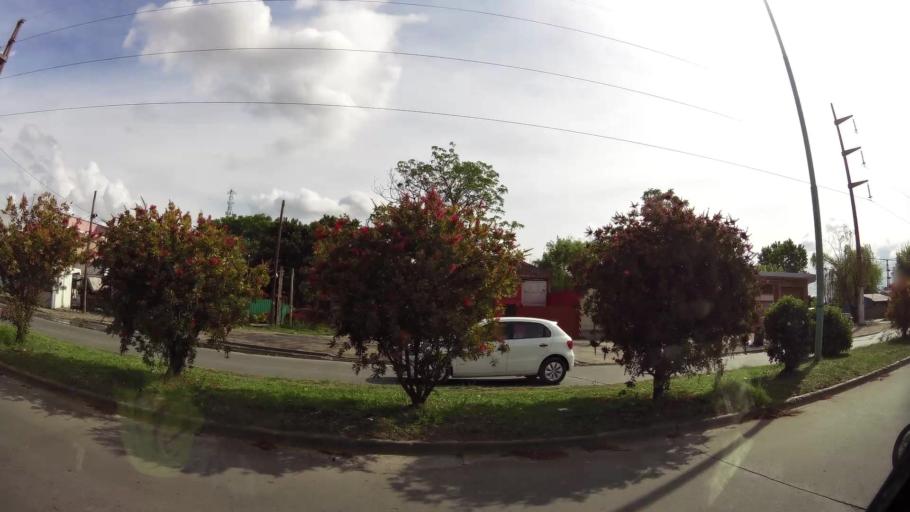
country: AR
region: Buenos Aires
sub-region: Partido de Quilmes
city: Quilmes
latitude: -34.7760
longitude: -58.2374
